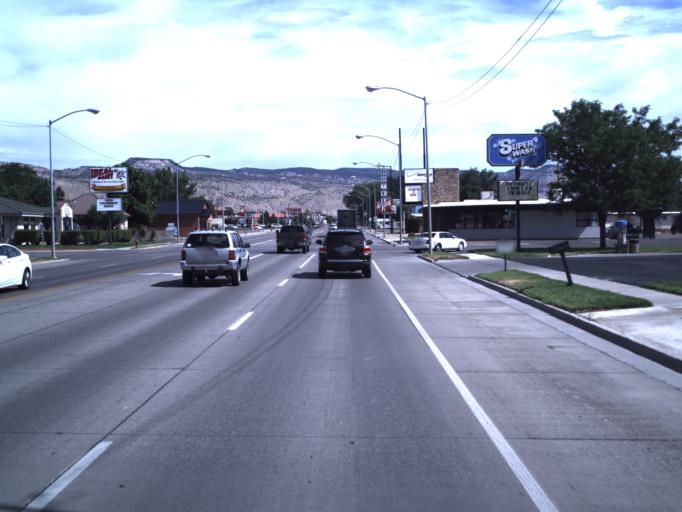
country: US
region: Utah
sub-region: Sevier County
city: Richfield
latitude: 38.7605
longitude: -112.0847
